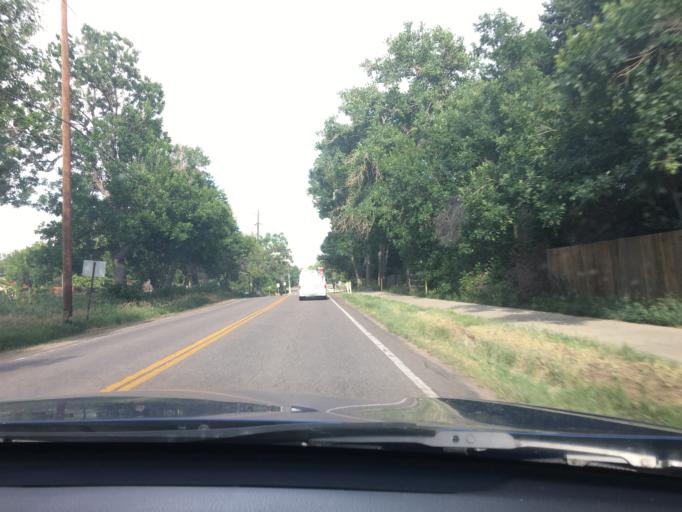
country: US
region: Colorado
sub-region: Jefferson County
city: Applewood
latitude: 39.7618
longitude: -105.1530
